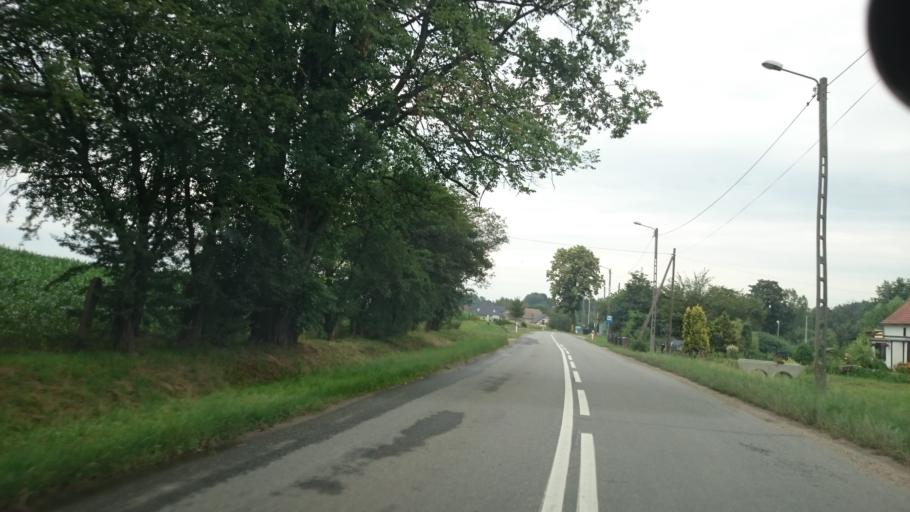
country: PL
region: Opole Voivodeship
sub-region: Powiat nyski
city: Kamiennik
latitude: 50.6243
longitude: 17.1273
